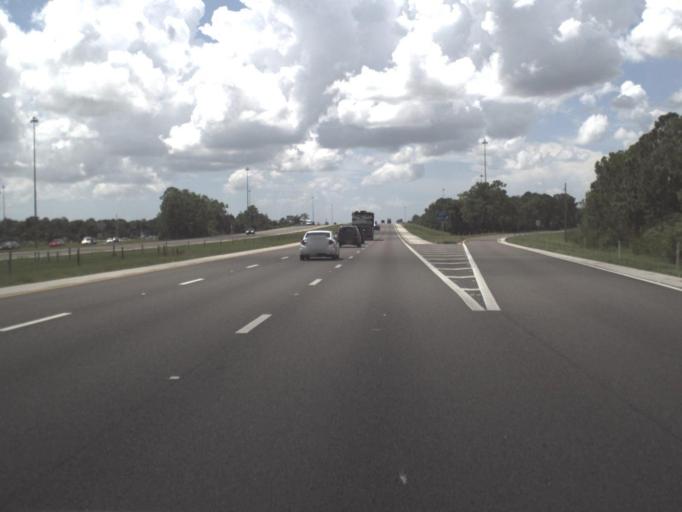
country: US
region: Florida
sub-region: Collier County
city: Vineyards
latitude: 26.2175
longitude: -81.7364
